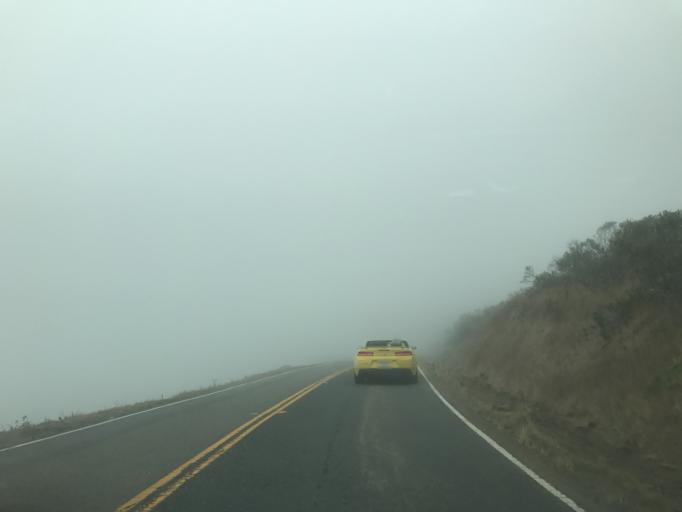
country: US
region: California
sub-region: Sonoma County
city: Monte Rio
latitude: 38.4763
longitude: -123.1579
